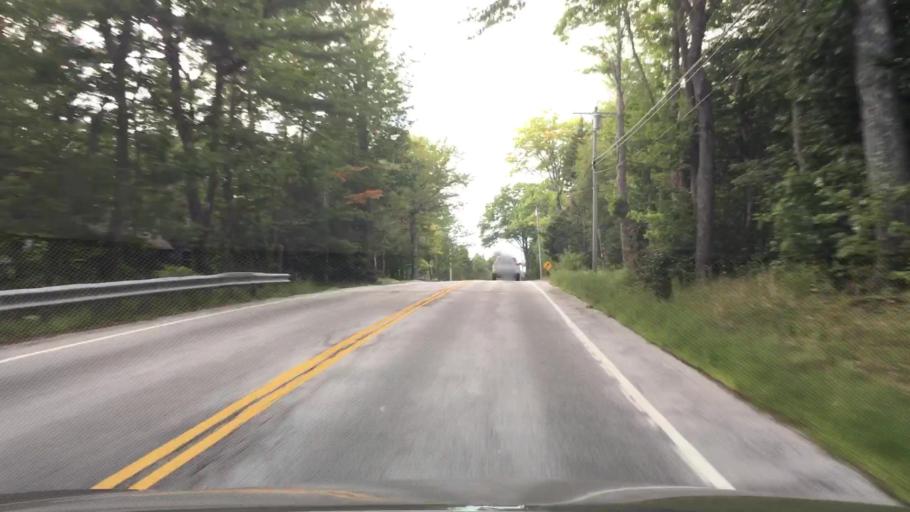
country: US
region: Maine
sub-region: Hancock County
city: Penobscot
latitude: 44.4265
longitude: -68.6012
